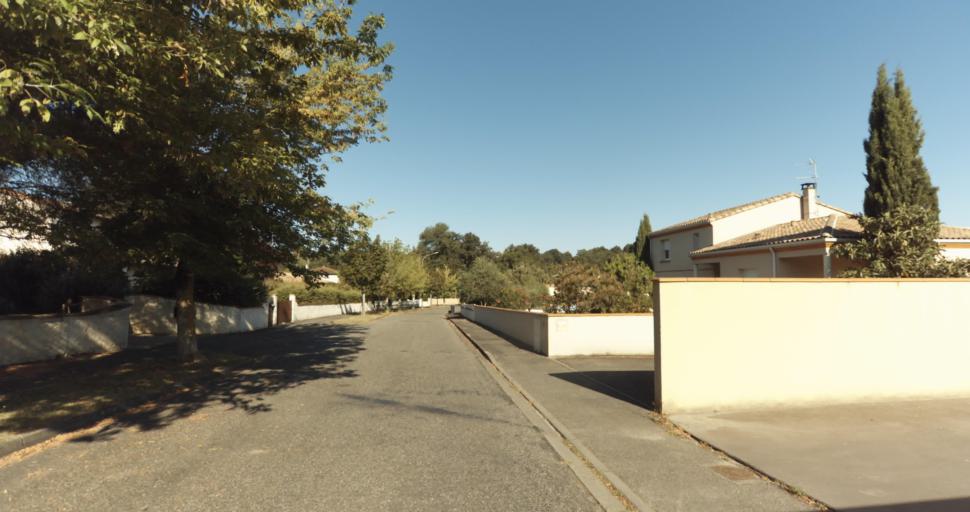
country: FR
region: Midi-Pyrenees
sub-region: Departement de la Haute-Garonne
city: L'Union
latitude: 43.6685
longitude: 1.4793
